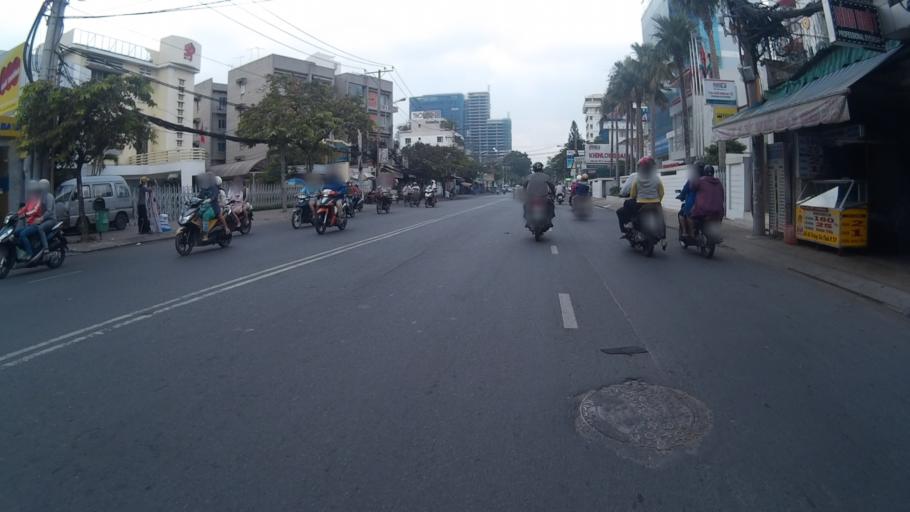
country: VN
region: Ho Chi Minh City
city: Quan Ba
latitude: 10.7762
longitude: 106.6850
